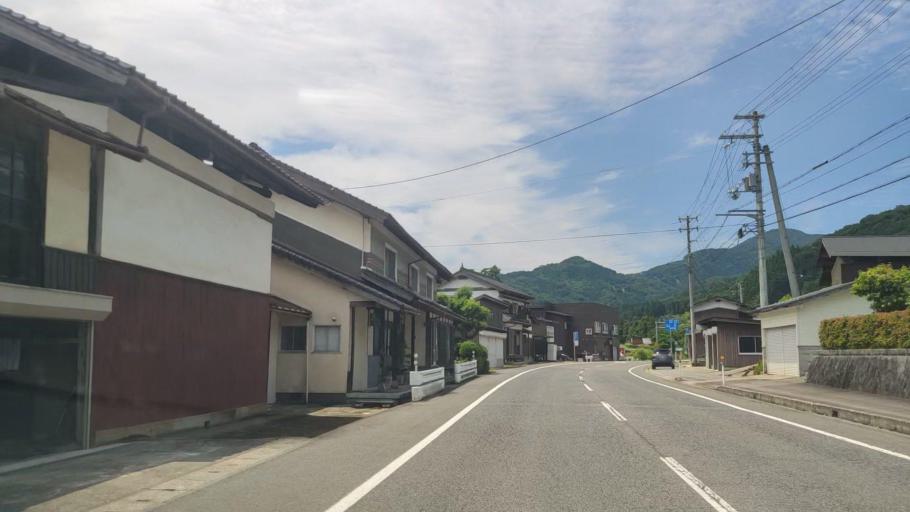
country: JP
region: Hyogo
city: Toyooka
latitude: 35.4631
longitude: 134.5433
